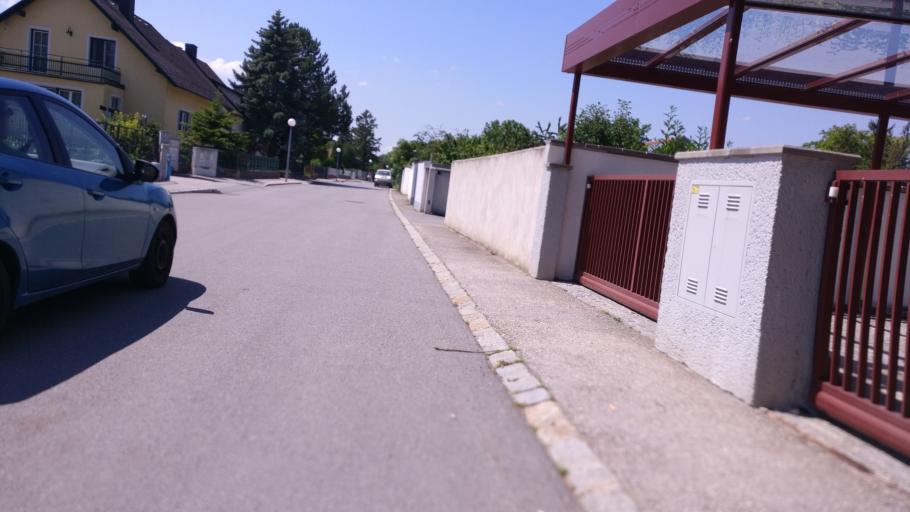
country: AT
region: Lower Austria
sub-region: Politischer Bezirk Baden
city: Oberwaltersdorf
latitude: 47.9782
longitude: 16.3253
